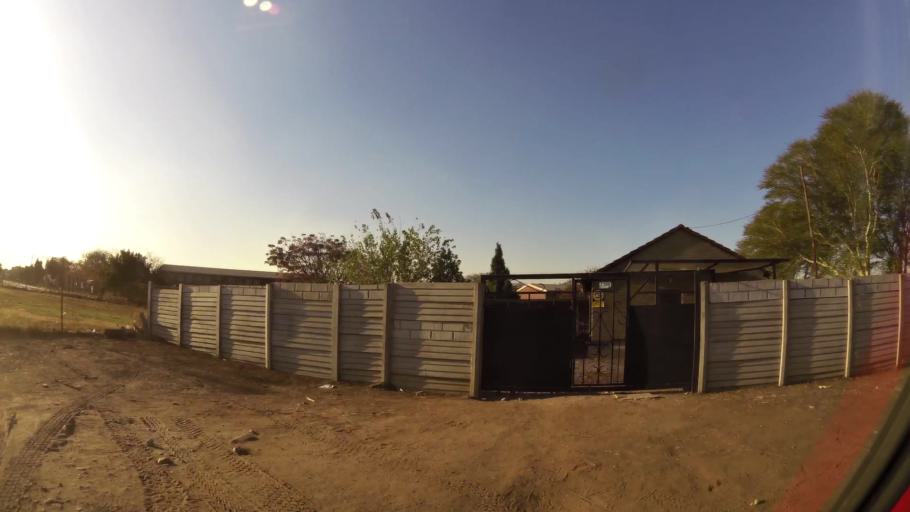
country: ZA
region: North-West
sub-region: Bojanala Platinum District Municipality
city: Rustenburg
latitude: -25.6443
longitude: 27.2275
